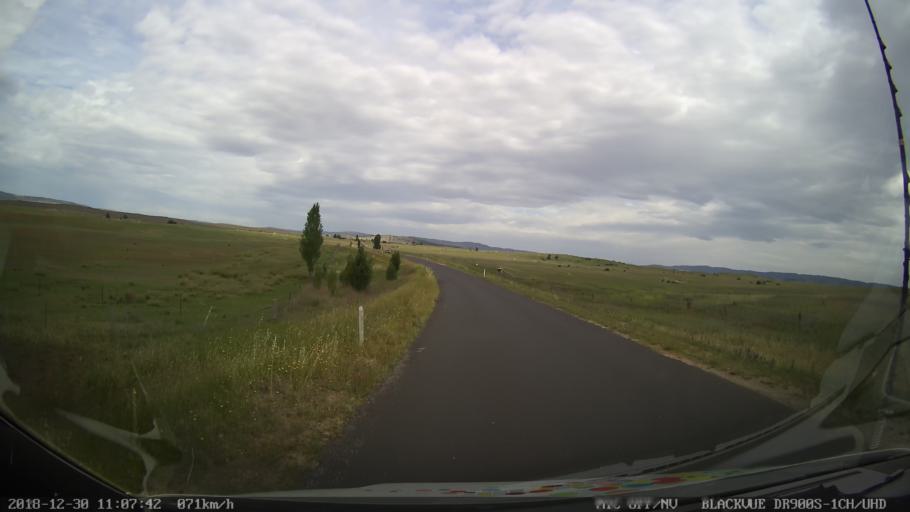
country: AU
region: New South Wales
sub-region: Snowy River
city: Berridale
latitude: -36.5015
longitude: 148.8167
